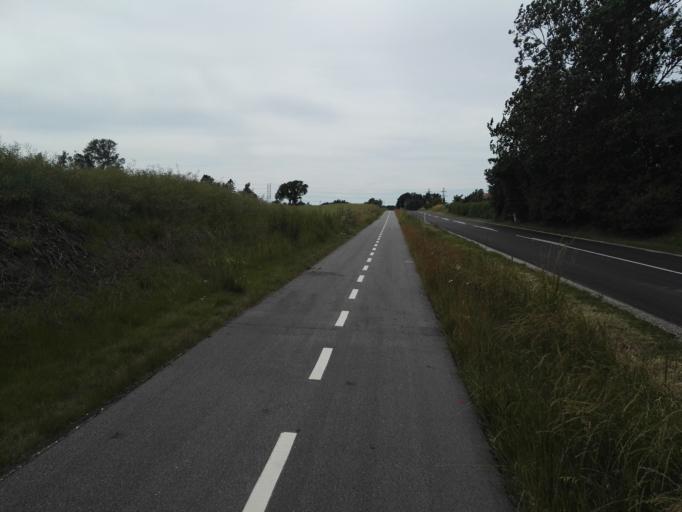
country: DK
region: Capital Region
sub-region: Hillerod Kommune
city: Skaevinge
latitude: 55.9152
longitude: 12.1802
